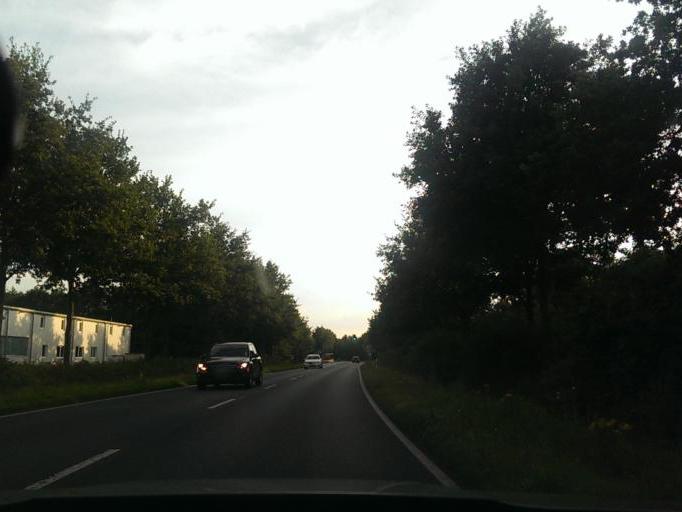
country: DE
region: Lower Saxony
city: Lilienthal
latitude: 53.1448
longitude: 8.9018
